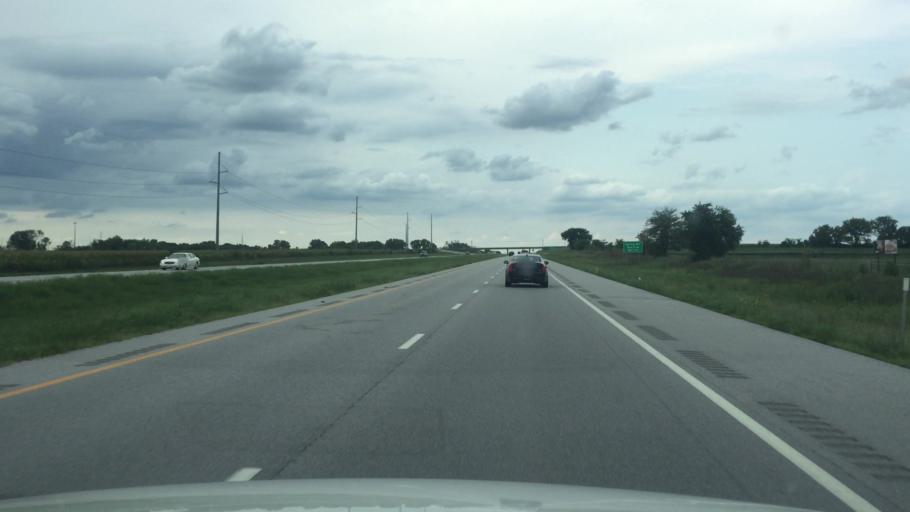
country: US
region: Kansas
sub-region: Miami County
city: Louisburg
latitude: 38.7157
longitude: -94.6763
